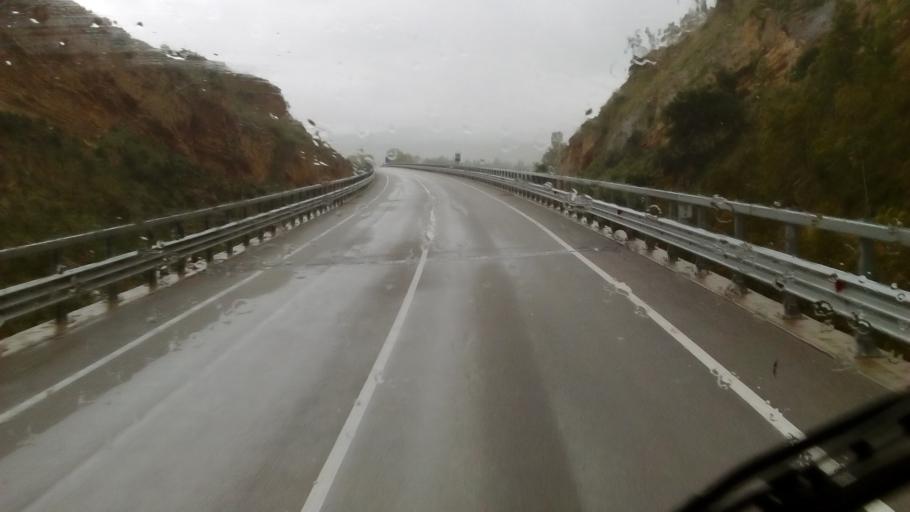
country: IT
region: Sicily
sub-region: Enna
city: Pietraperzia
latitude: 37.4984
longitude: 14.1424
